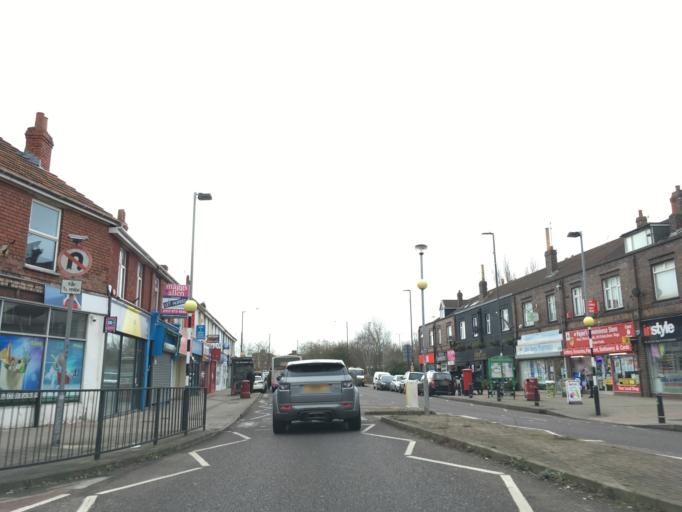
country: GB
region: England
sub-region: South Gloucestershire
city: Stoke Gifford
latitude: 51.5015
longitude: -2.5793
